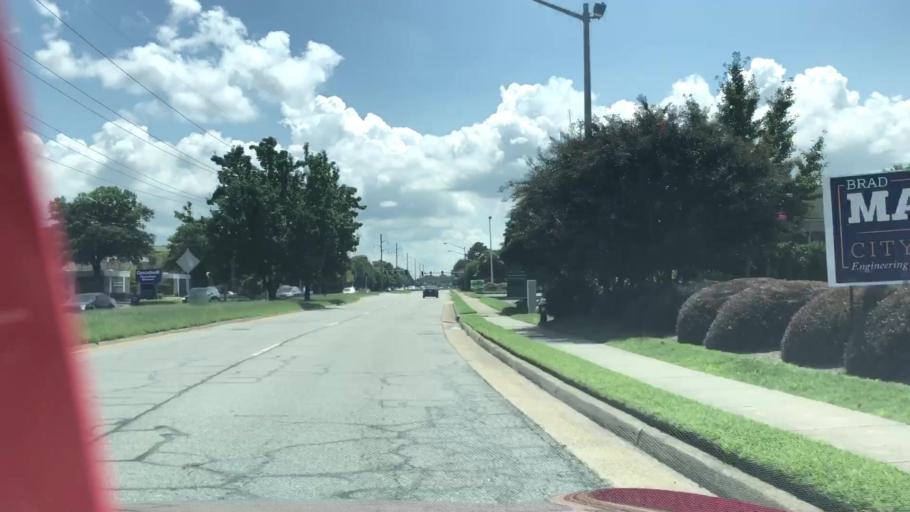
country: US
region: Virginia
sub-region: City of Virginia Beach
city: Virginia Beach
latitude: 36.8678
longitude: -76.0302
